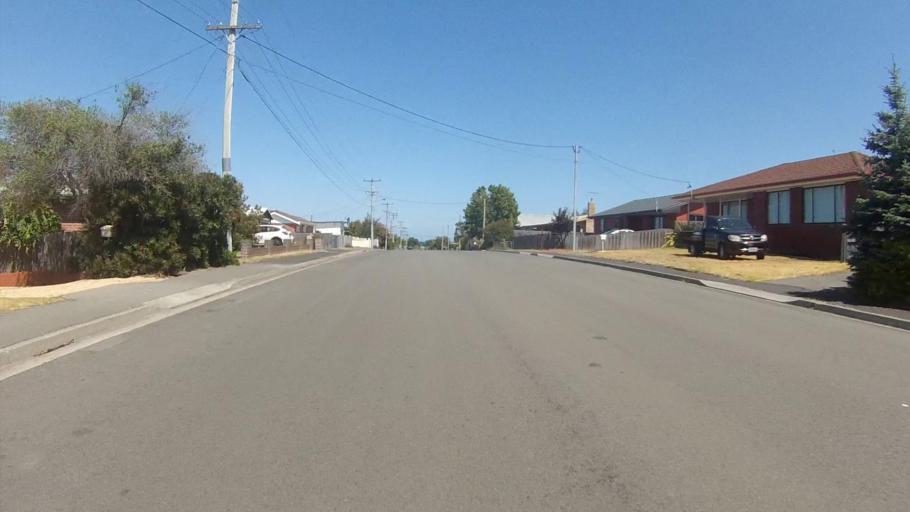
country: AU
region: Tasmania
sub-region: Sorell
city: Sorell
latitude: -42.7997
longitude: 147.5339
